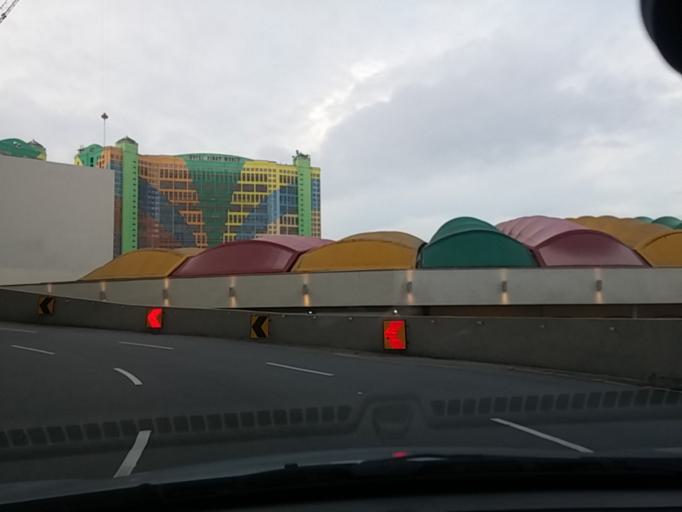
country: MY
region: Pahang
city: Kampung Bukit Tinggi, Bentong
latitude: 3.4223
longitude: 101.7933
